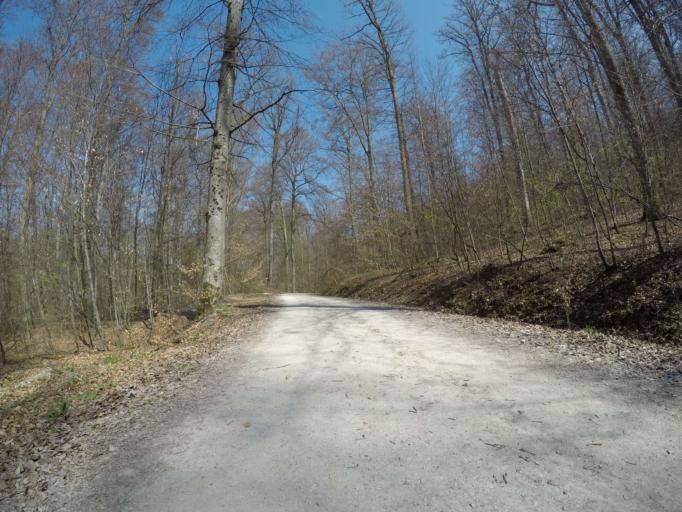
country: DE
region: Baden-Wuerttemberg
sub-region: Tuebingen Region
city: Gomaringen
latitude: 48.4625
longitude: 9.1350
